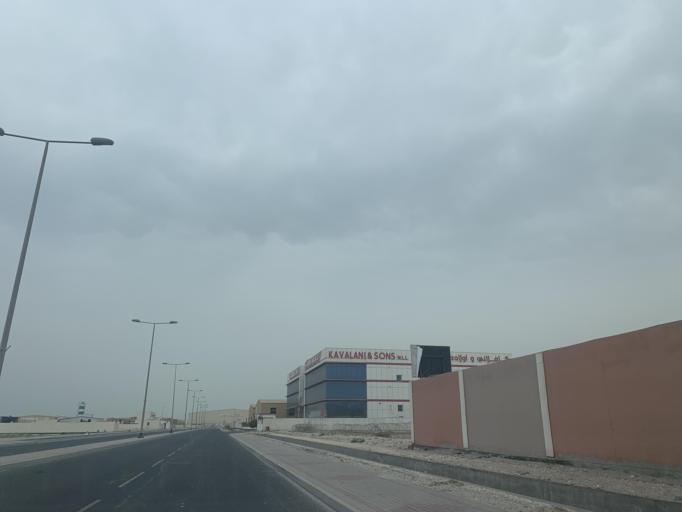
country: BH
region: Muharraq
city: Al Hadd
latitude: 26.2094
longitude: 50.6825
